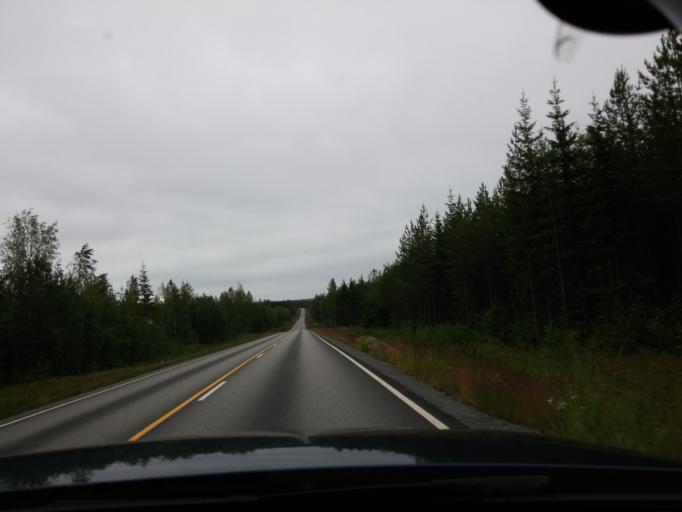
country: FI
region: Central Finland
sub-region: Saarijaervi-Viitasaari
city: Saarijaervi
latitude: 62.6793
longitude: 25.1941
